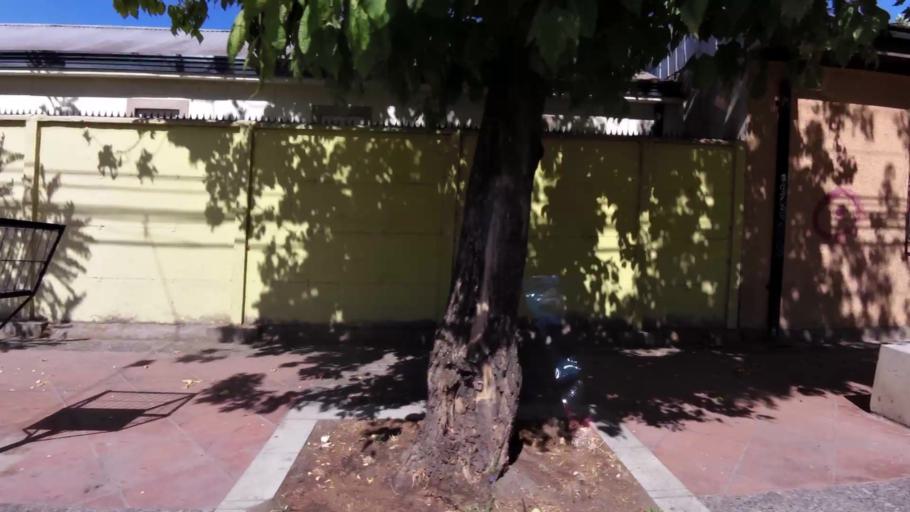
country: CL
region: Maule
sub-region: Provincia de Talca
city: Talca
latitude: -35.4193
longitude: -71.6591
